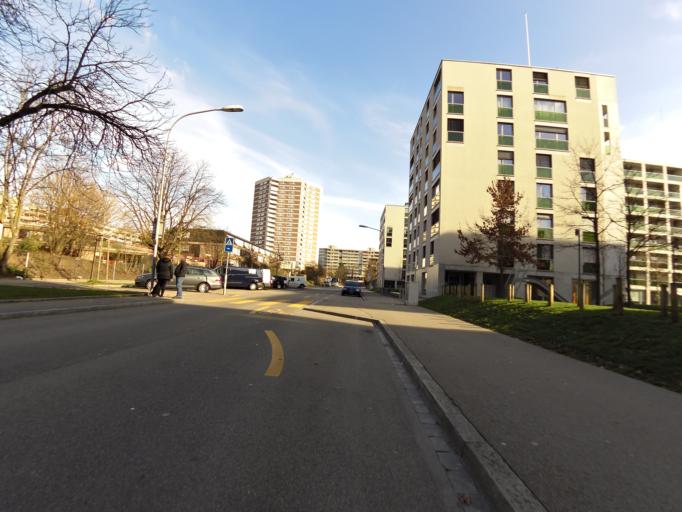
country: CH
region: Zurich
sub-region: Bezirk Zuerich
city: Zuerich (Kreis 9) / Altstetten
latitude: 47.3964
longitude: 8.4873
